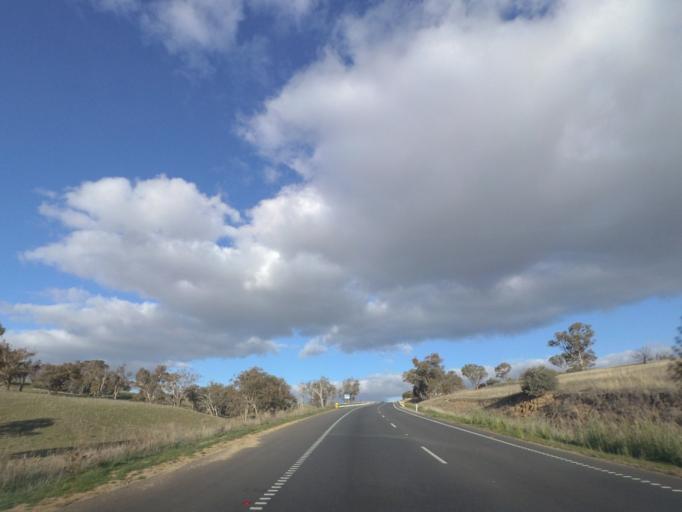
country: AU
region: New South Wales
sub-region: Gundagai
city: Gundagai
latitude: -34.8134
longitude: 148.4289
